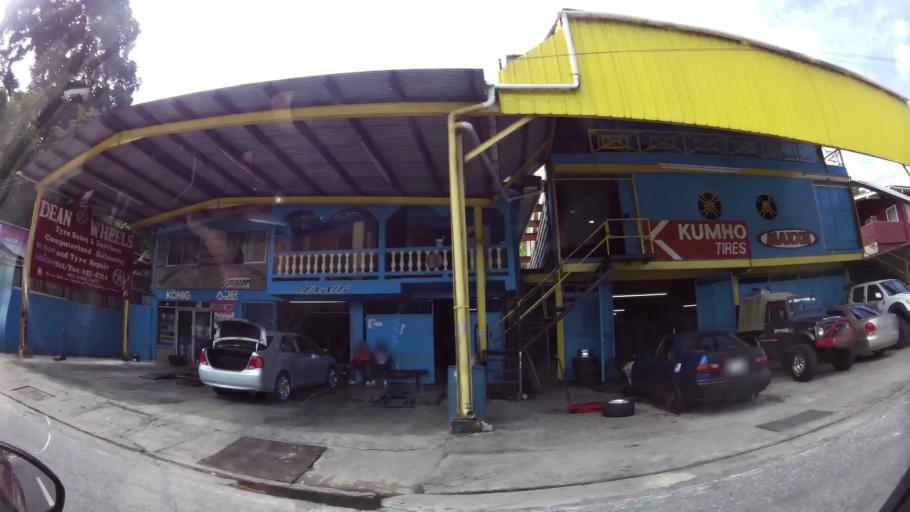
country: TT
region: Diego Martin
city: Petit Valley
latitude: 10.7070
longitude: -61.5573
